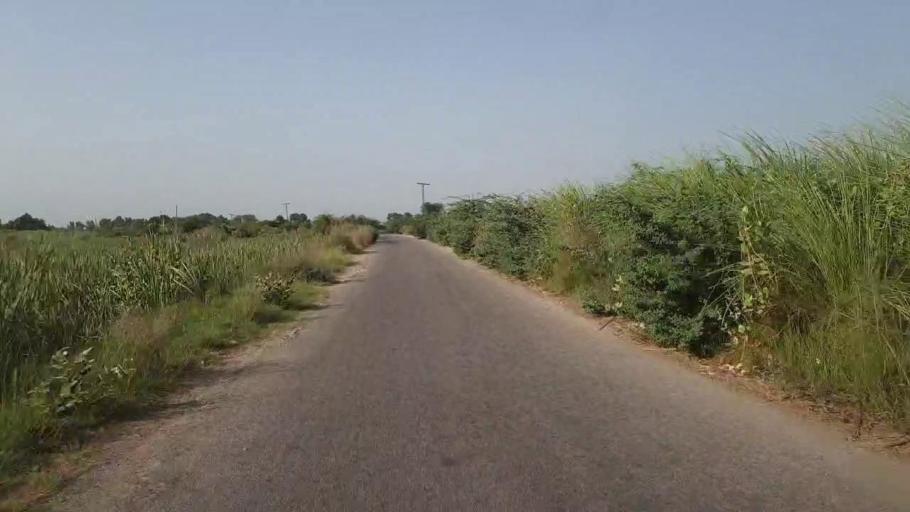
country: PK
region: Sindh
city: Jam Sahib
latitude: 26.4220
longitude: 68.8712
